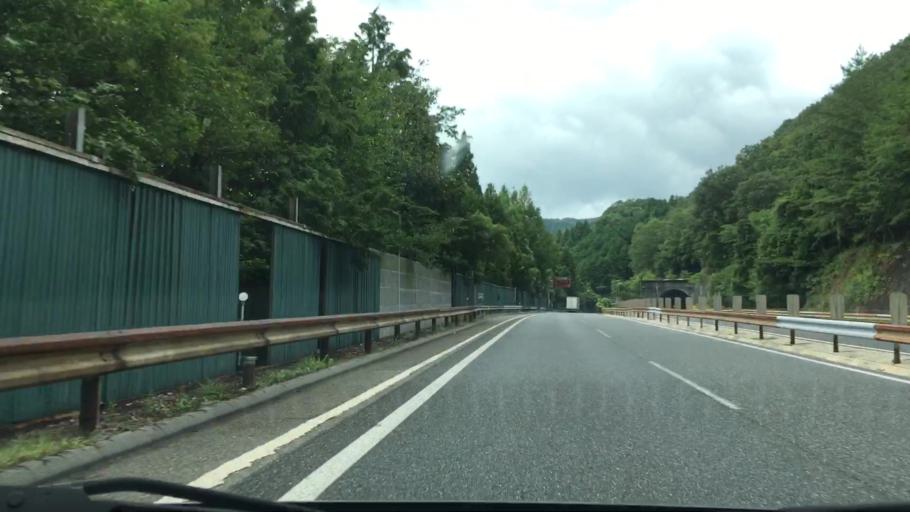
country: JP
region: Okayama
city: Niimi
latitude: 34.9660
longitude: 133.6427
